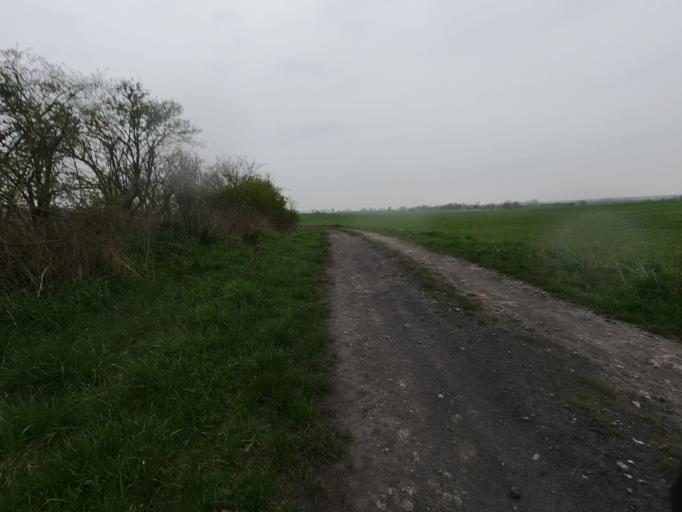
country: PL
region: West Pomeranian Voivodeship
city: Trzcinsko Zdroj
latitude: 52.9216
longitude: 14.7315
